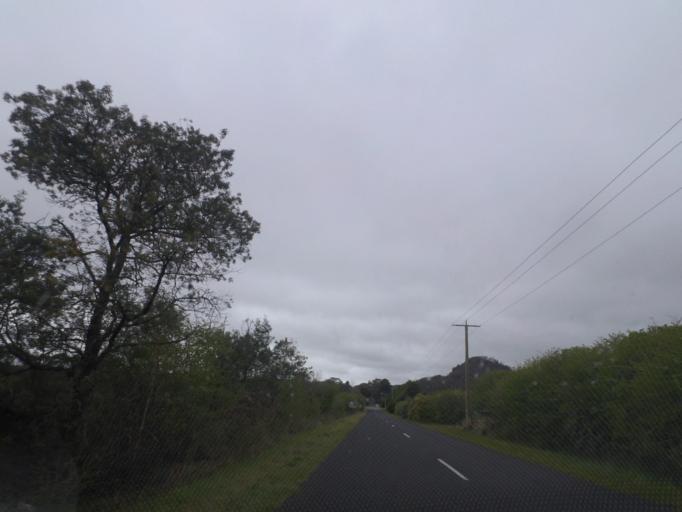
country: AU
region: Victoria
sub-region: Hume
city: Sunbury
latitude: -37.3263
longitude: 144.5839
